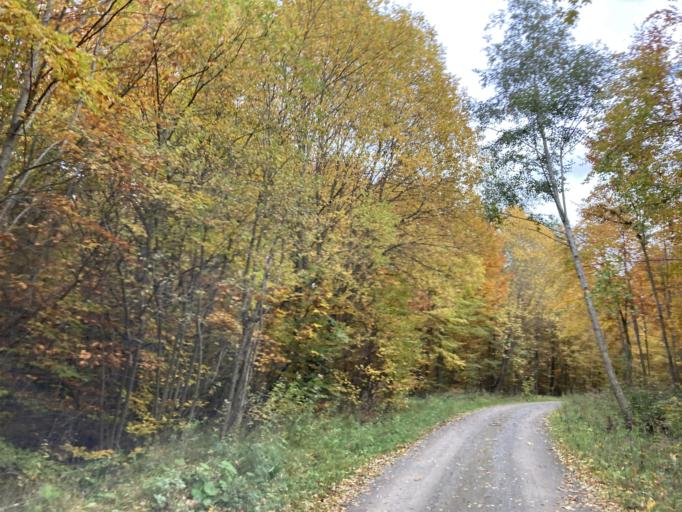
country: DE
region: Baden-Wuerttemberg
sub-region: Tuebingen Region
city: Dusslingen
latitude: 48.4618
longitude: 9.0214
